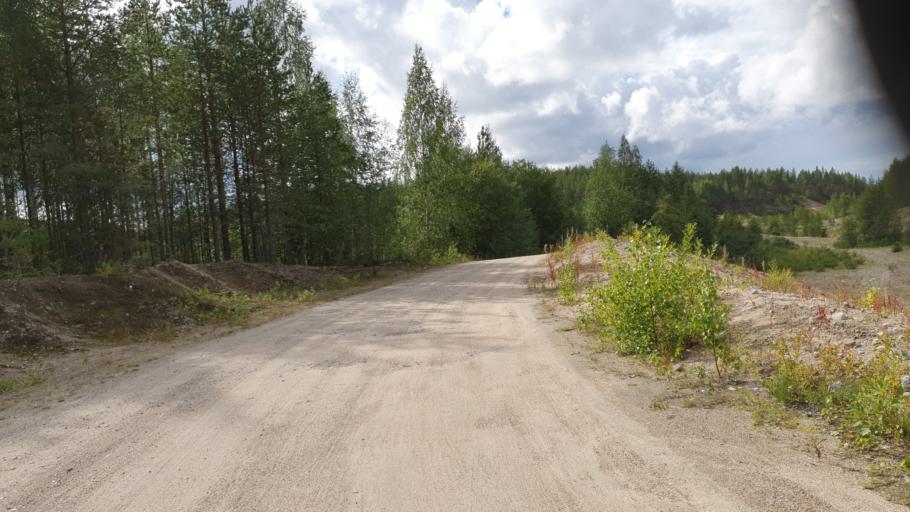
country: FI
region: Kainuu
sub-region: Kehys-Kainuu
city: Kuhmo
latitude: 64.1536
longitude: 29.3904
